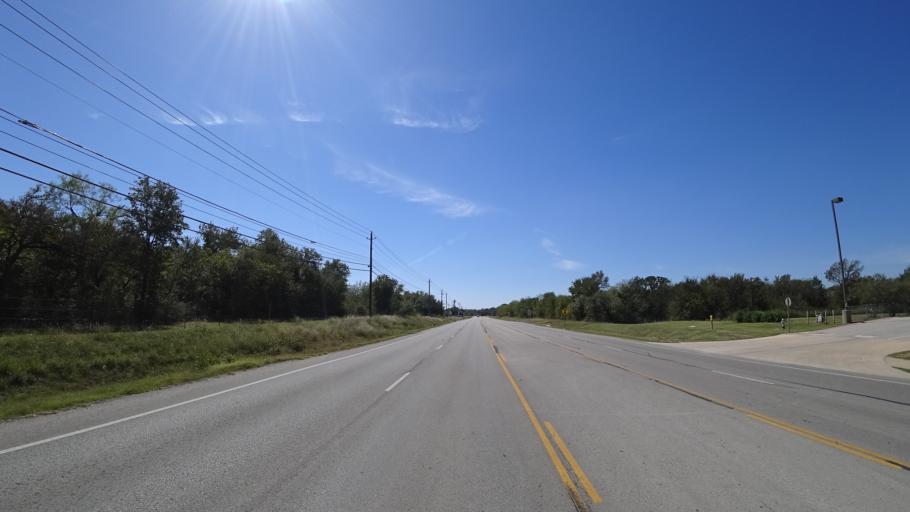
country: US
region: Texas
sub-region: Travis County
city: Hornsby Bend
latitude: 30.2799
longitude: -97.6352
